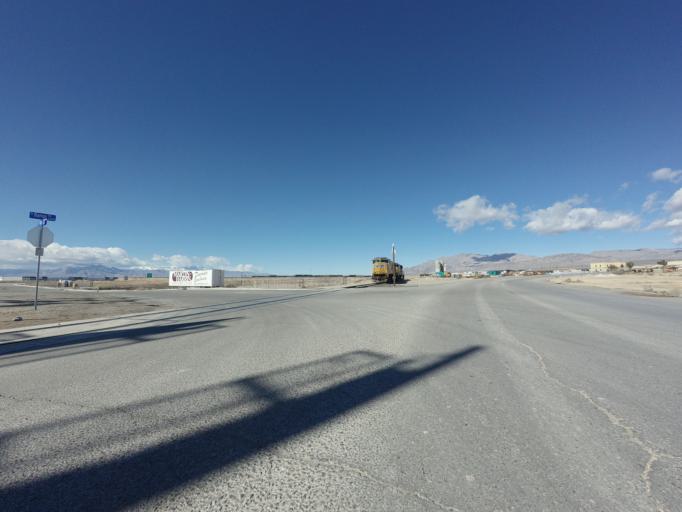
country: US
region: Nevada
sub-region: Clark County
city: Nellis Air Force Base
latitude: 36.2704
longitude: -115.0620
